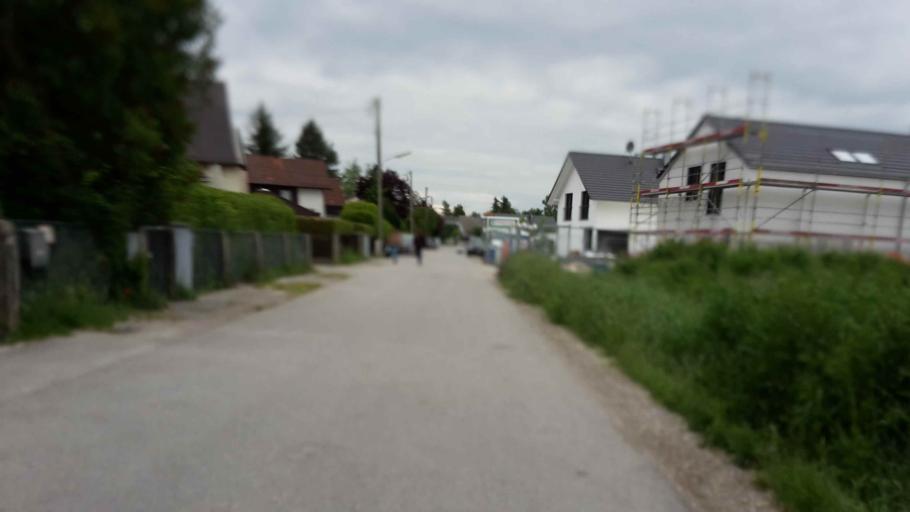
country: DE
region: Bavaria
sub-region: Upper Bavaria
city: Grobenzell
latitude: 48.1826
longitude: 11.4180
